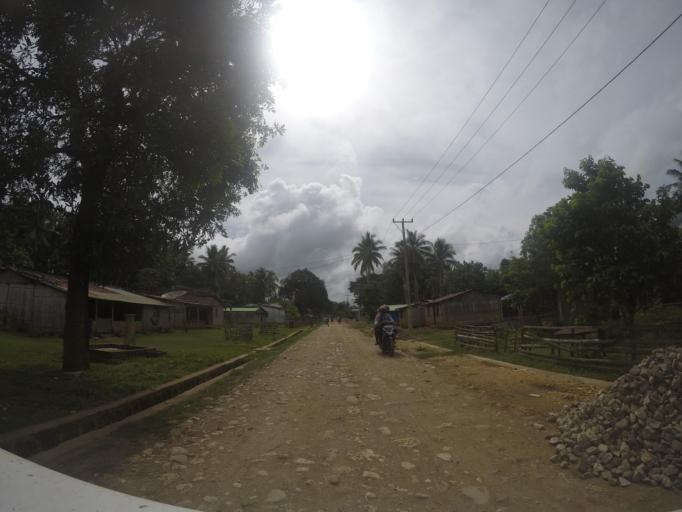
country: TL
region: Lautem
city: Lospalos
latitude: -8.5023
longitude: 126.9674
